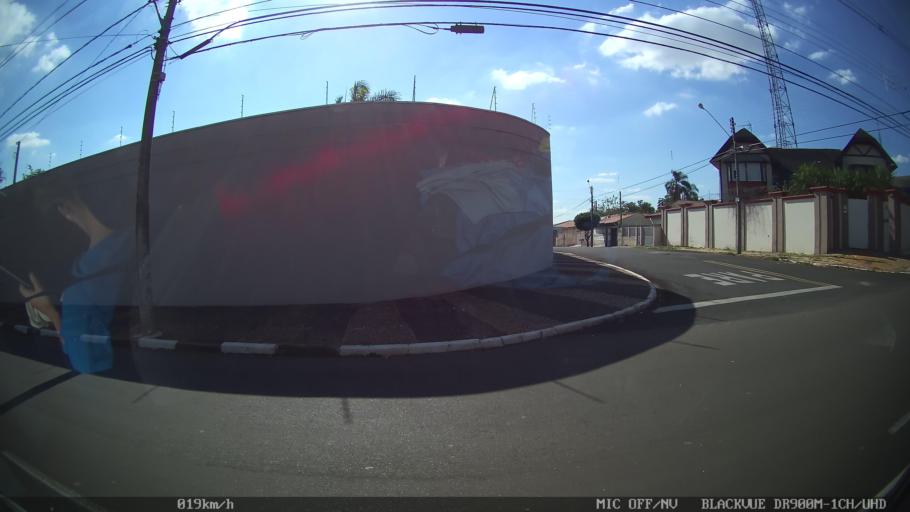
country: BR
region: Sao Paulo
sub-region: Sumare
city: Sumare
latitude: -22.8226
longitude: -47.2765
